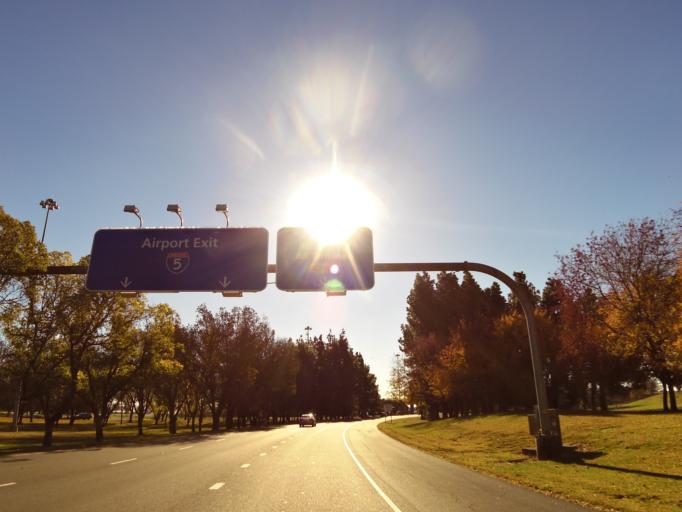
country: US
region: California
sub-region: Yolo County
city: West Sacramento
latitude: 38.6813
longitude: -121.5922
